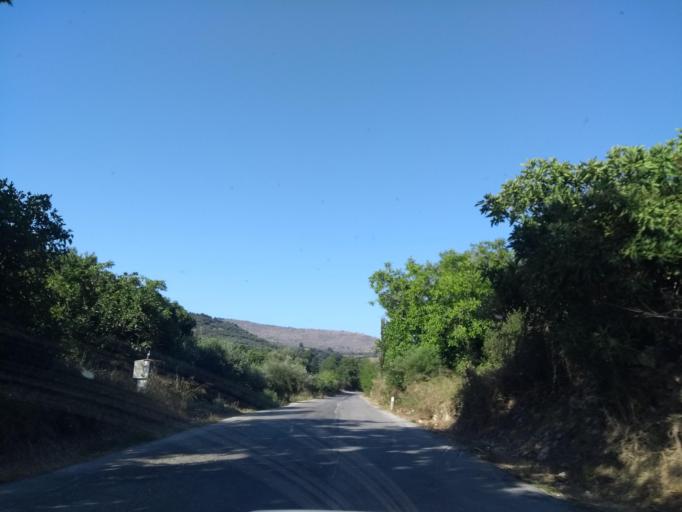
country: GR
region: Crete
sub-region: Nomos Chanias
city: Georgioupolis
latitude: 35.3646
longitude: 24.2218
